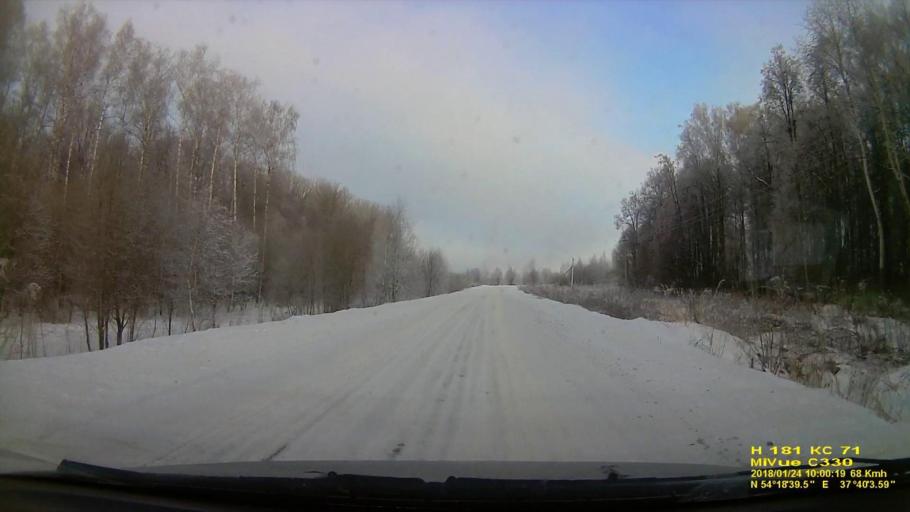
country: RU
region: Tula
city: Revyakino
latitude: 54.3111
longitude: 37.6676
